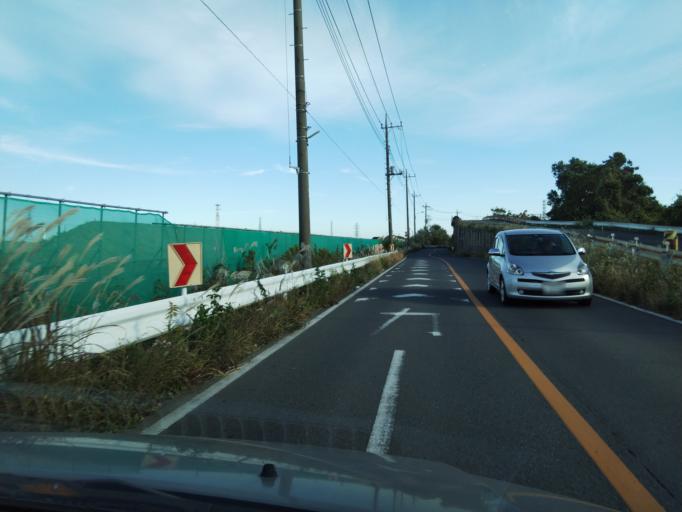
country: JP
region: Saitama
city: Yoshikawa
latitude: 35.8707
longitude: 139.8553
